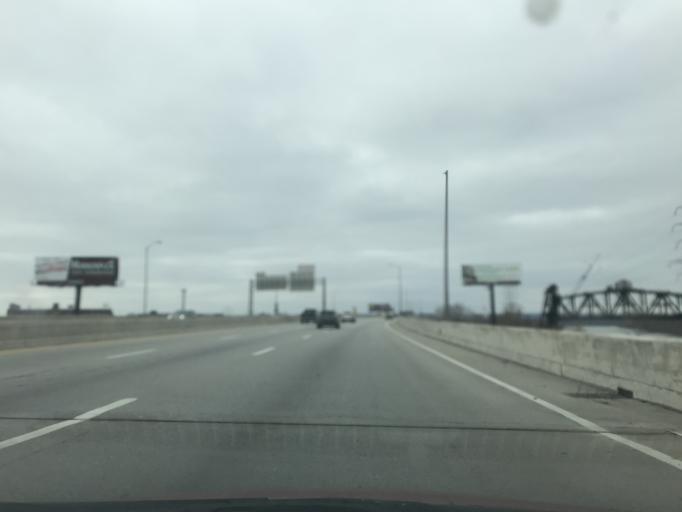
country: US
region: Kentucky
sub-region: Jefferson County
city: Louisville
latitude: 38.2609
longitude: -85.7691
